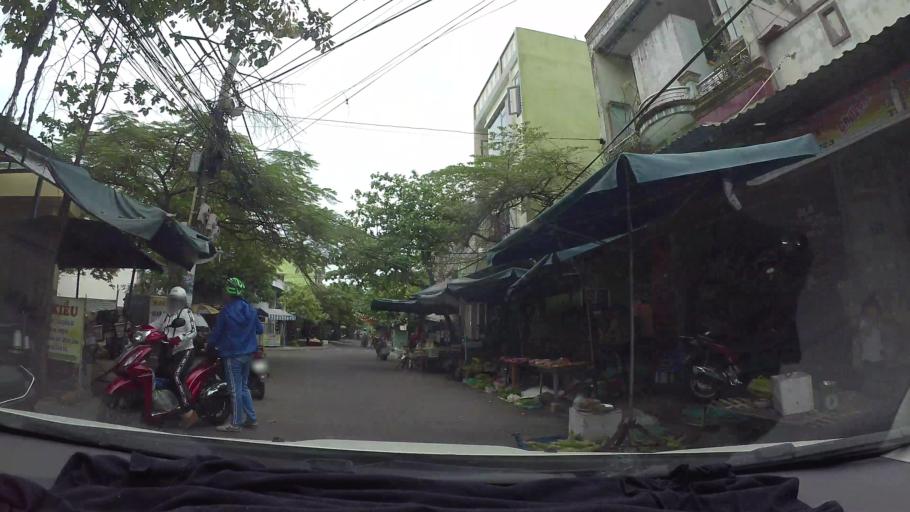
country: VN
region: Da Nang
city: Lien Chieu
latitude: 16.0749
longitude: 108.1727
